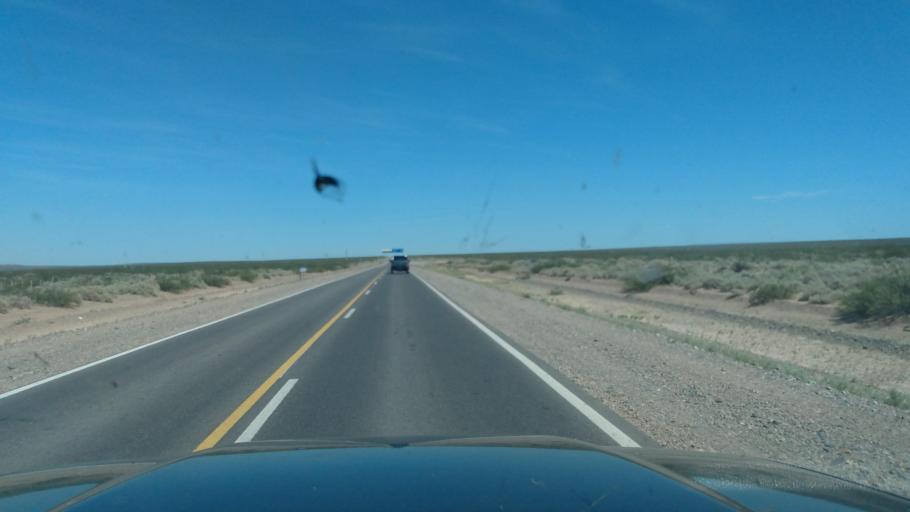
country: AR
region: Neuquen
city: Senillosa
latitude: -39.0714
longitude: -68.6093
